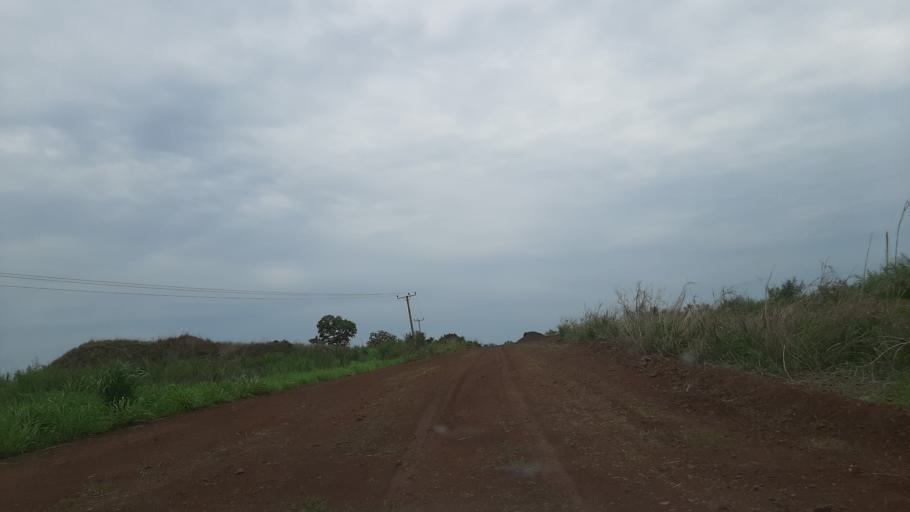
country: ET
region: Gambela
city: Gambela
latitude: 8.2189
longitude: 34.5251
